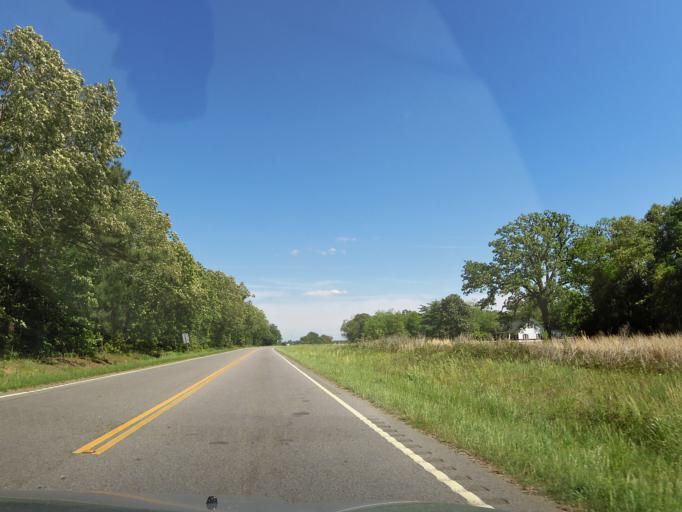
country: US
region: South Carolina
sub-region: Aiken County
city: Aiken
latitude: 33.5377
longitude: -81.6542
